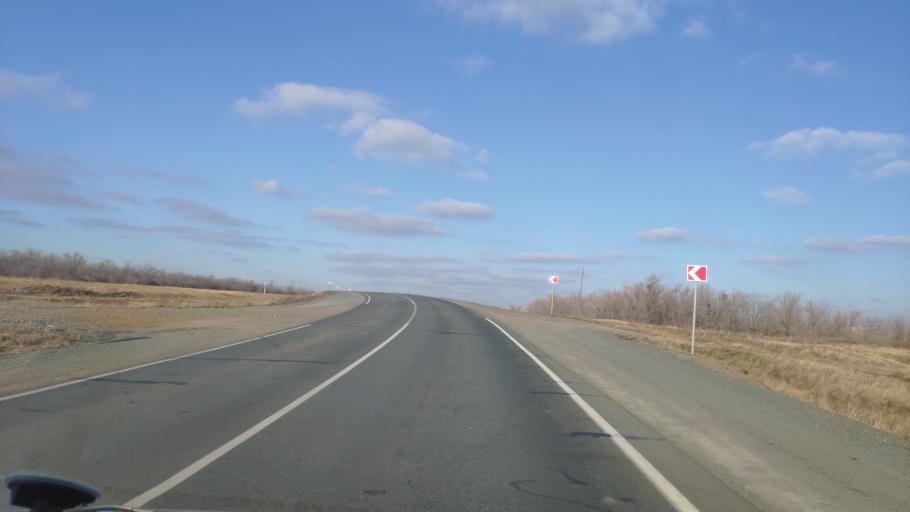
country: RU
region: Orenburg
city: Gay
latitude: 51.4243
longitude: 58.4095
